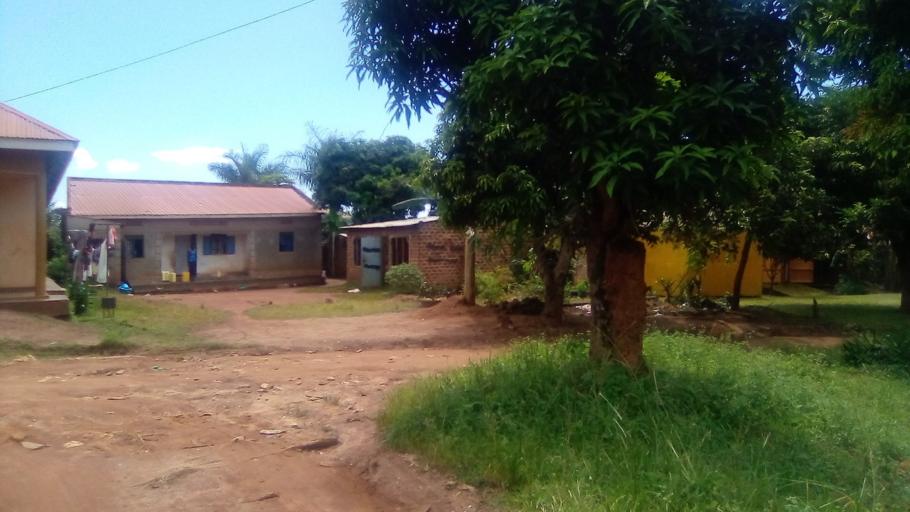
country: UG
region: Central Region
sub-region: Wakiso District
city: Entebbe
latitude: 0.0981
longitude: 32.5289
